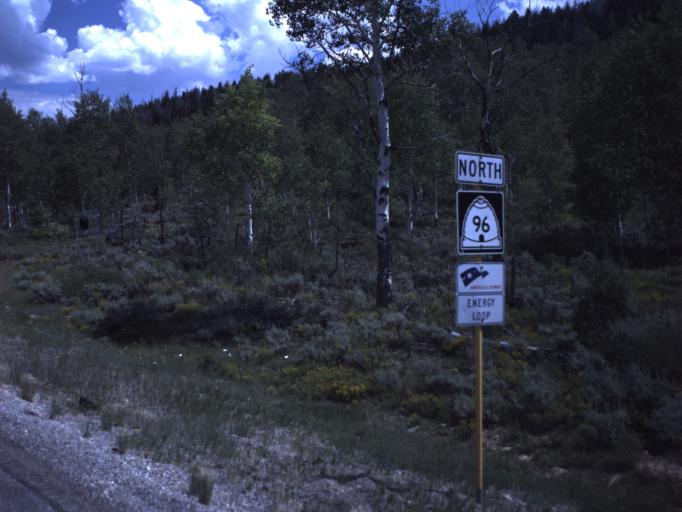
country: US
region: Utah
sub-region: Carbon County
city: Helper
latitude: 39.8537
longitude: -111.1269
